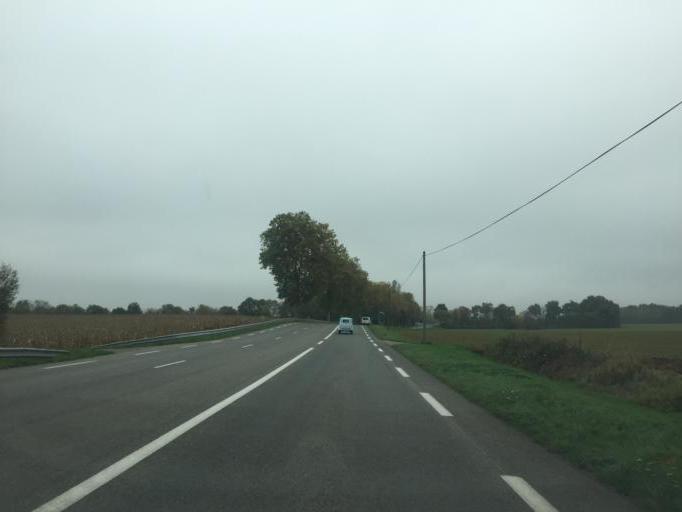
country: FR
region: Rhone-Alpes
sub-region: Departement de l'Ain
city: Villars-les-Dombes
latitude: 45.9797
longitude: 5.0134
